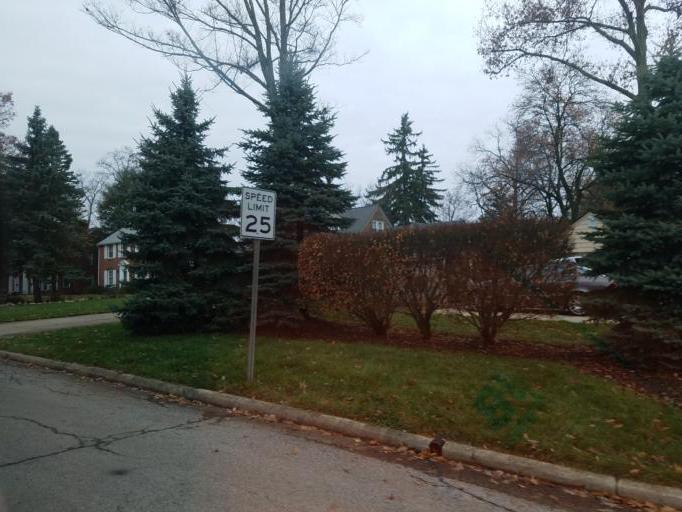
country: US
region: Ohio
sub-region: Richland County
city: Mansfield
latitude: 40.7376
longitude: -82.5310
